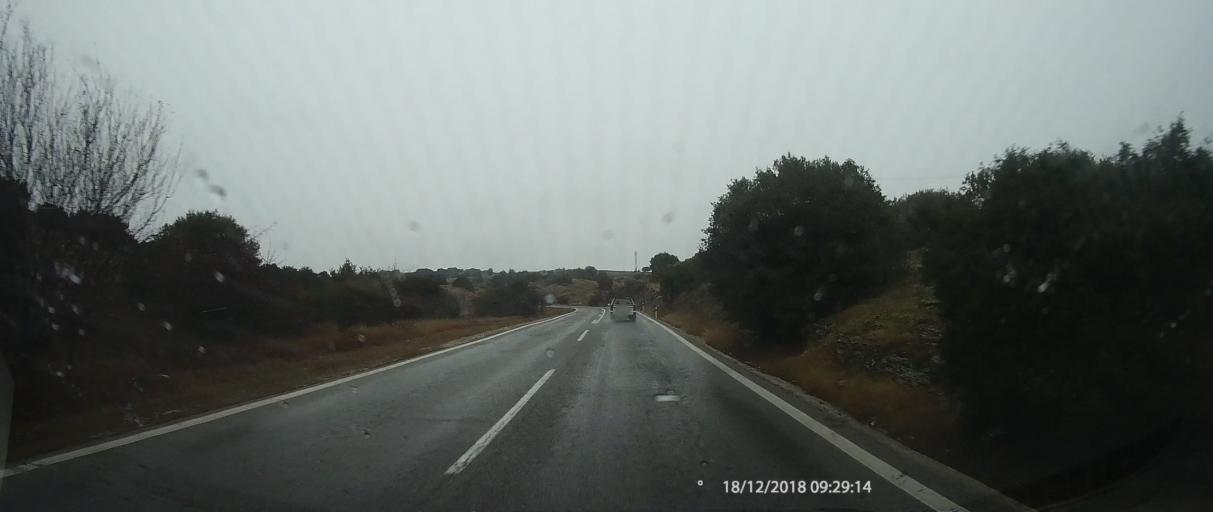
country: GR
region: Thessaly
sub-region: Nomos Larisis
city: Elassona
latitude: 39.9262
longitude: 22.1716
